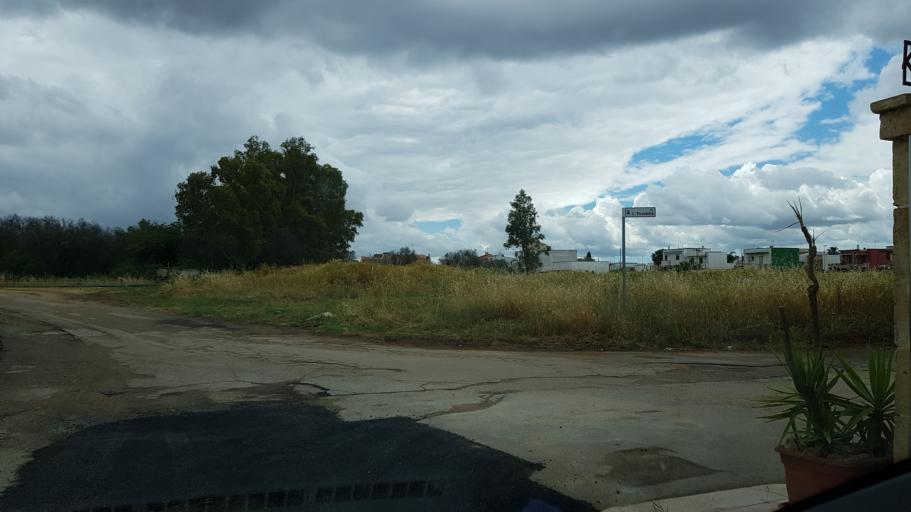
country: IT
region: Apulia
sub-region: Provincia di Brindisi
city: Torchiarolo
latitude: 40.4906
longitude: 18.0507
